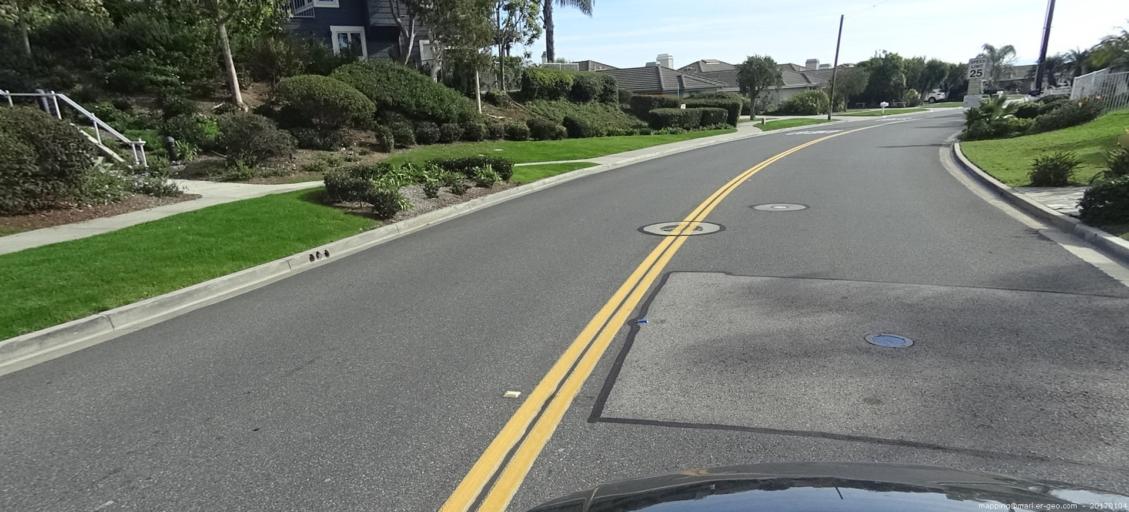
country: US
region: California
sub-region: Orange County
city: Dana Point
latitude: 33.4691
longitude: -117.6887
